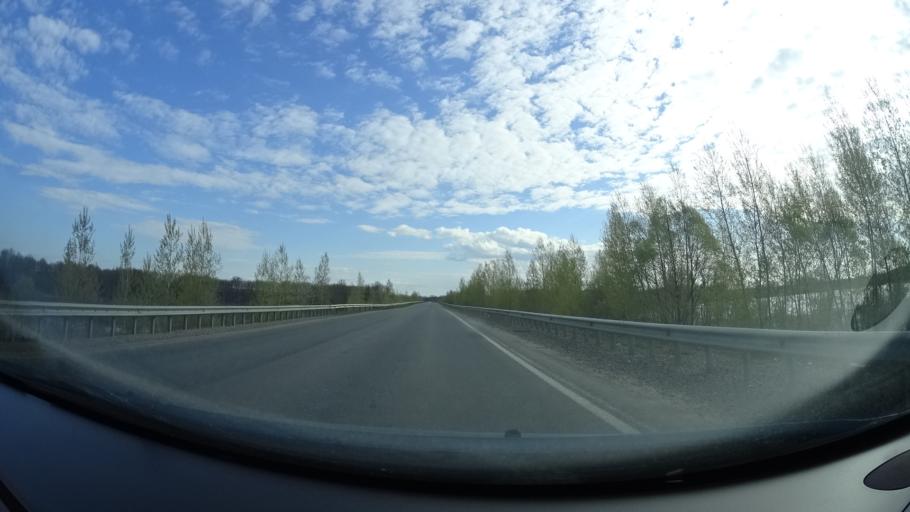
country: RU
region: Bashkortostan
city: Blagoveshchensk
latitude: 55.0228
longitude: 55.7911
